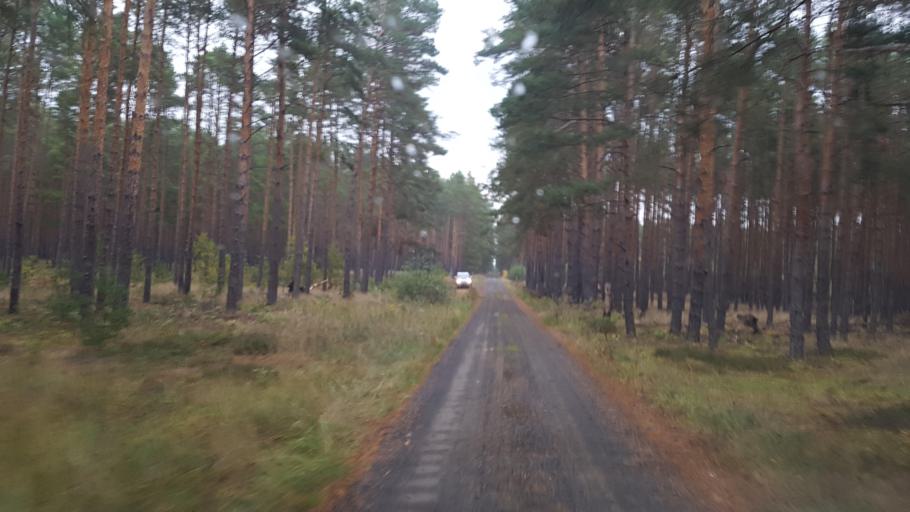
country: DE
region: Brandenburg
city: Schlieben
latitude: 51.7457
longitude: 13.3946
